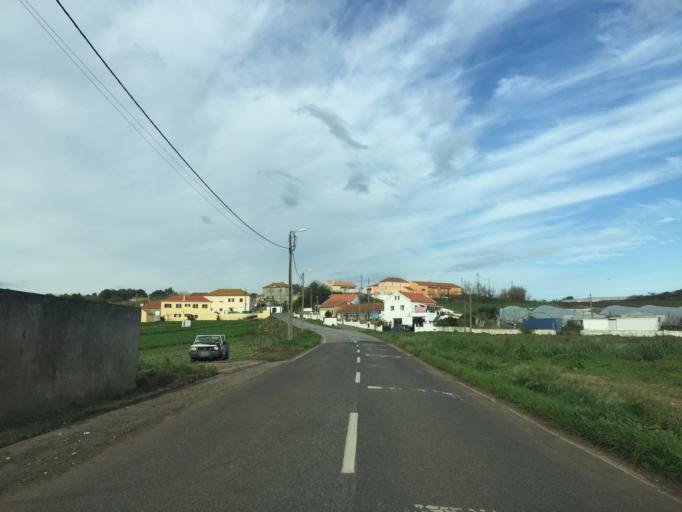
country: PT
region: Lisbon
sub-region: Sintra
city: Almargem
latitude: 38.8664
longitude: -9.2833
